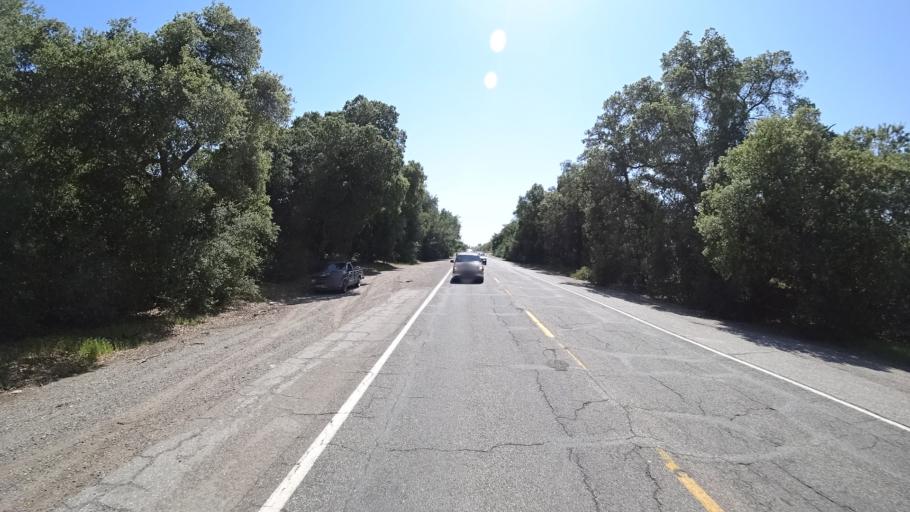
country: US
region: California
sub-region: Glenn County
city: Orland
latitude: 39.7990
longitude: -122.1973
